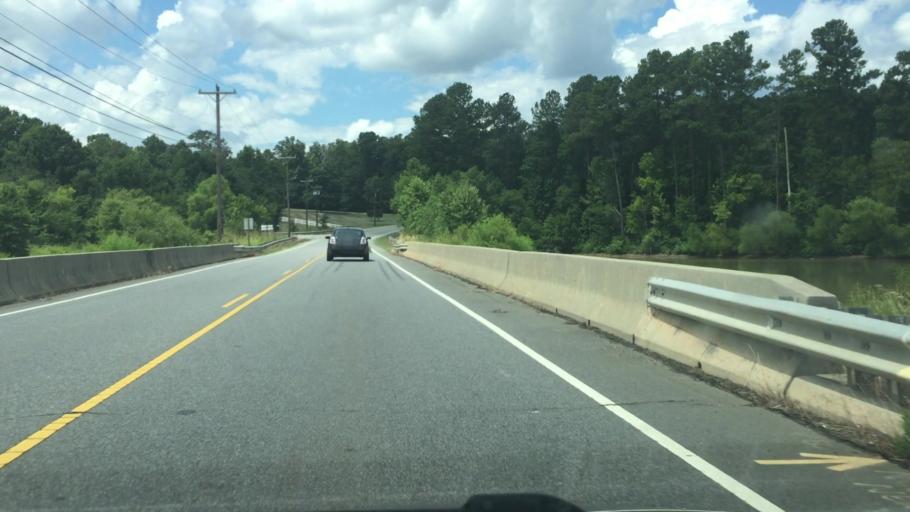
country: US
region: North Carolina
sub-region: Rowan County
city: Enochville
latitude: 35.4814
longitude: -80.7158
